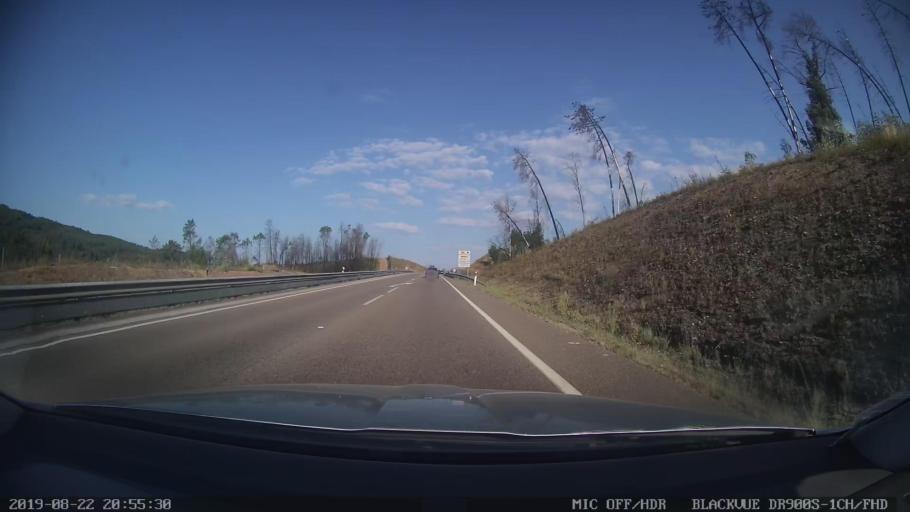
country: PT
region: Castelo Branco
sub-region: Serta
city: Serta
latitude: 39.7808
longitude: -8.0346
